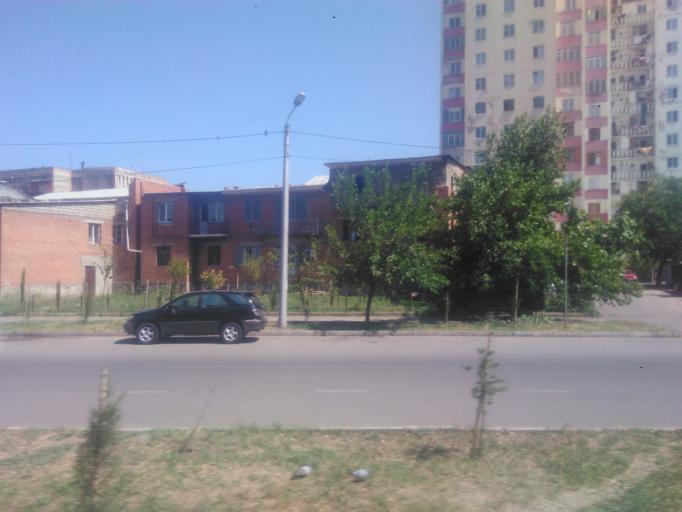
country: GE
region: T'bilisi
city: Tbilisi
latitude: 41.7080
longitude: 44.8831
